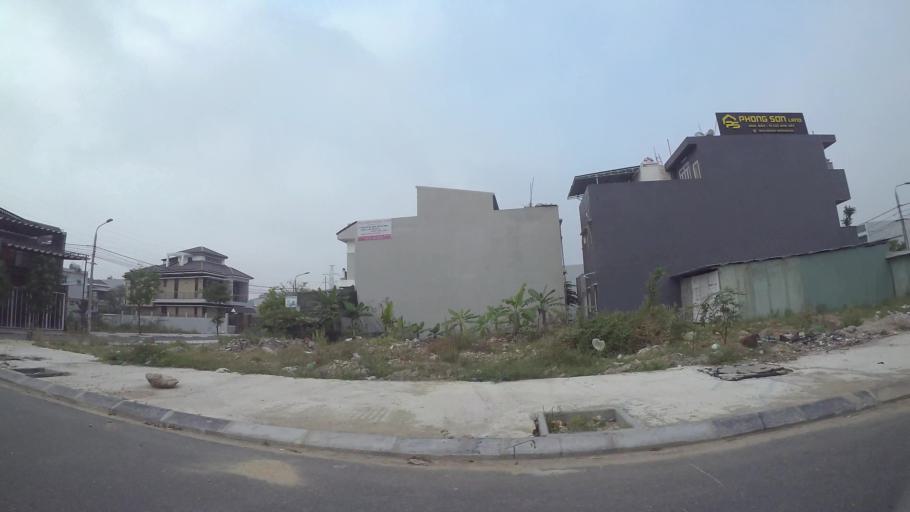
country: VN
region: Da Nang
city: Cam Le
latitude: 16.0129
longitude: 108.2234
